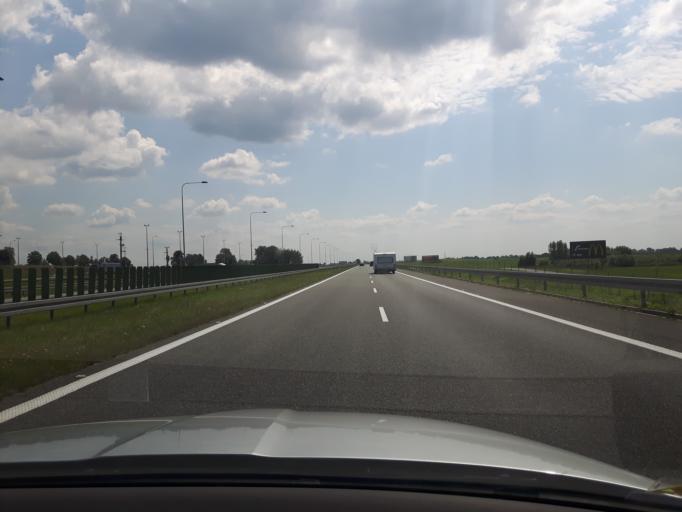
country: PL
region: Warmian-Masurian Voivodeship
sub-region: Powiat ostrodzki
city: Milomlyn
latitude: 53.8082
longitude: 19.7858
